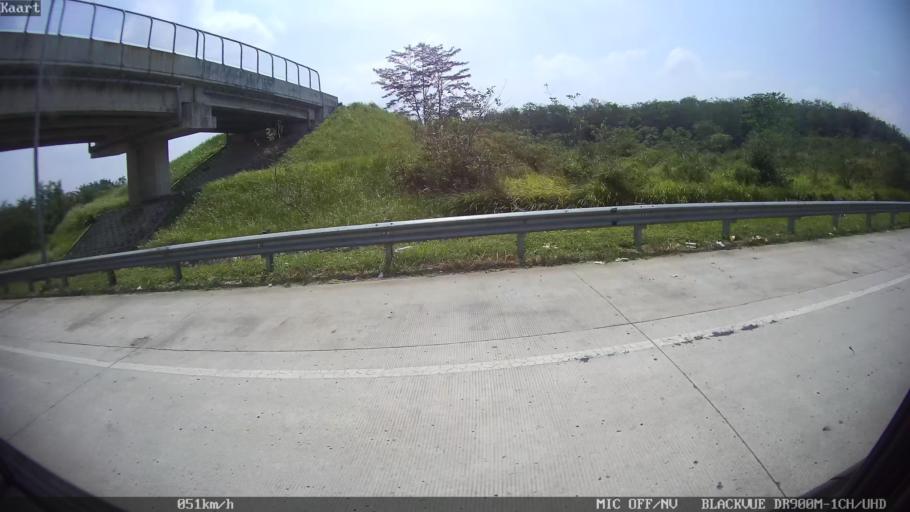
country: ID
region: Lampung
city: Kedaton
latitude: -5.3686
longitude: 105.3268
